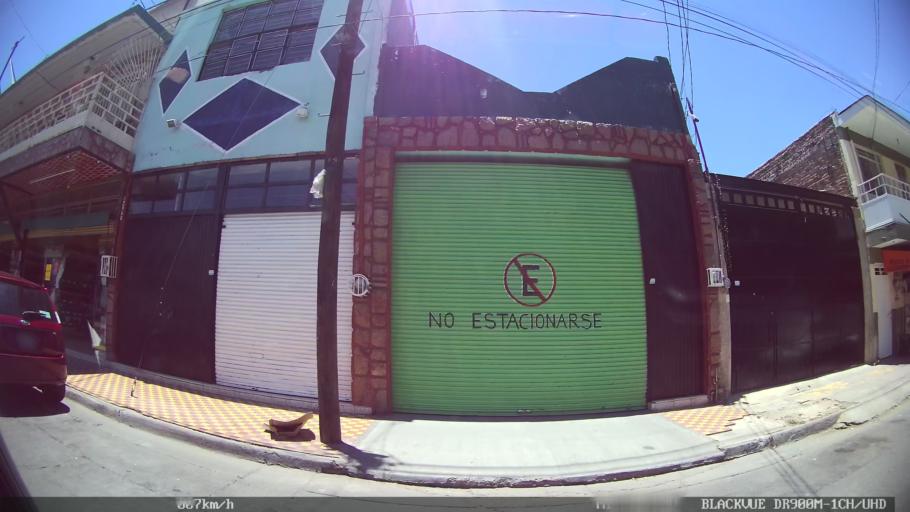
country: MX
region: Jalisco
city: Tlaquepaque
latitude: 20.6658
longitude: -103.2900
